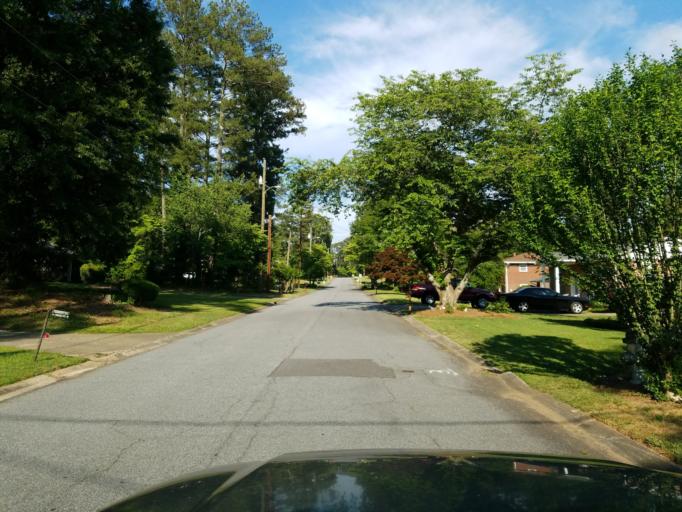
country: US
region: Georgia
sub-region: Cobb County
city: Smyrna
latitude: 33.9332
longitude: -84.4852
